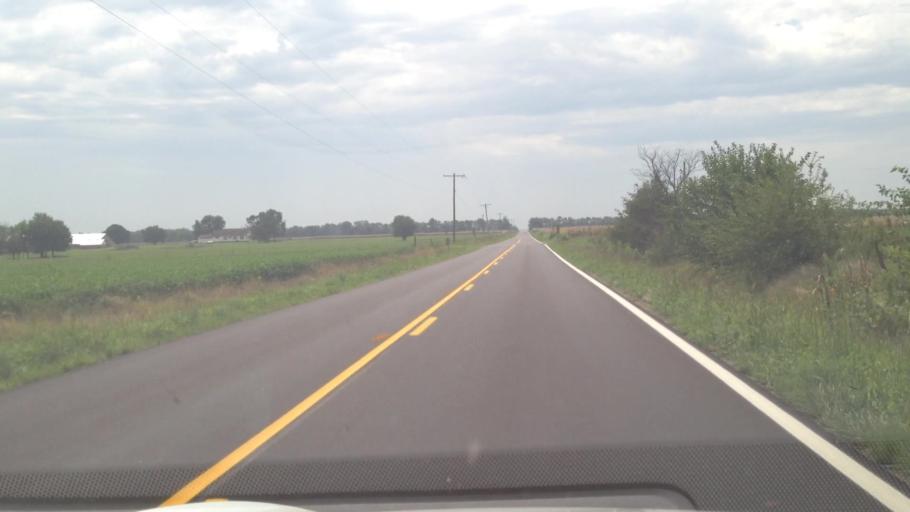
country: US
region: Kansas
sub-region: Crawford County
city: Girard
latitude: 37.6468
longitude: -94.9698
